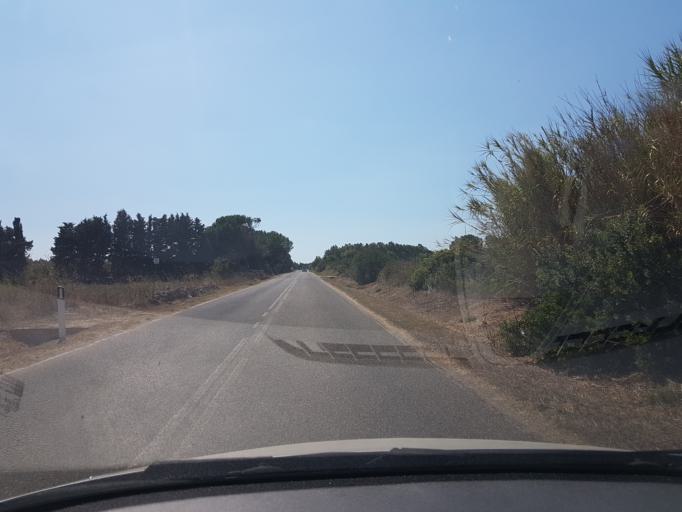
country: IT
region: Sardinia
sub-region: Provincia di Oristano
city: Riola Sardo
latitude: 39.9967
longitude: 8.4801
